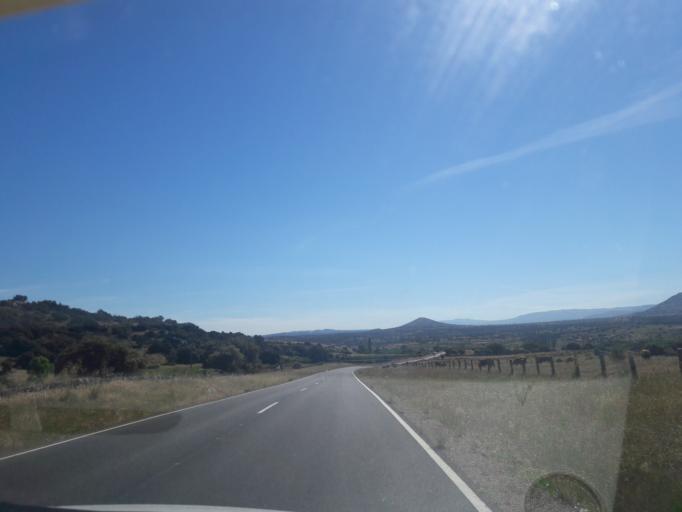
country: ES
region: Castille and Leon
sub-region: Provincia de Salamanca
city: Santibanez de Bejar
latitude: 40.4813
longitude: -5.6323
